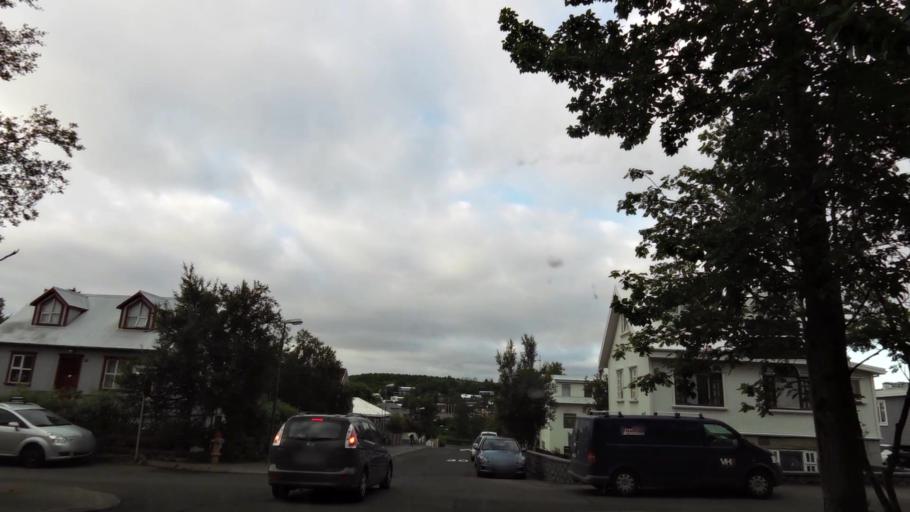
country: IS
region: Capital Region
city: Hafnarfjoerdur
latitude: 64.0645
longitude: -21.9424
